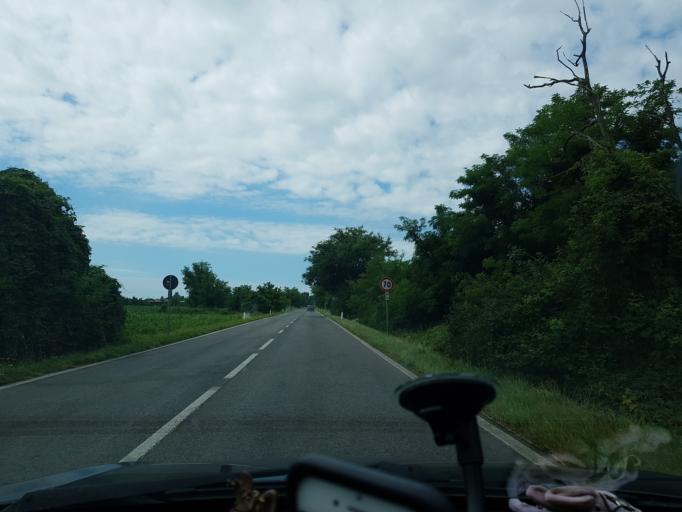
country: IT
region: Friuli Venezia Giulia
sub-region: Provincia di Gorizia
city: Turriaco
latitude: 45.8314
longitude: 13.4409
